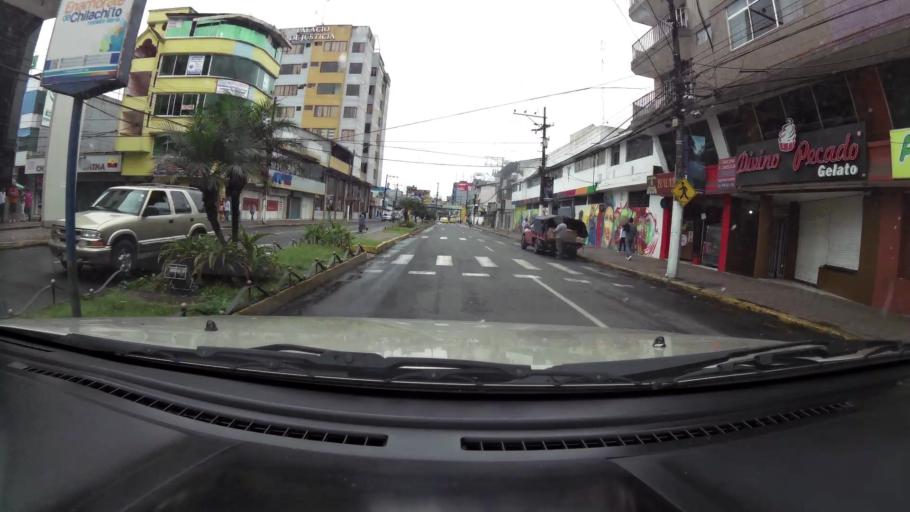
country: EC
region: Santo Domingo de los Tsachilas
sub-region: Canton Santo Domingo de los Colorados
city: Santo Domingo de los Colorados
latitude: -0.2528
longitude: -79.1657
